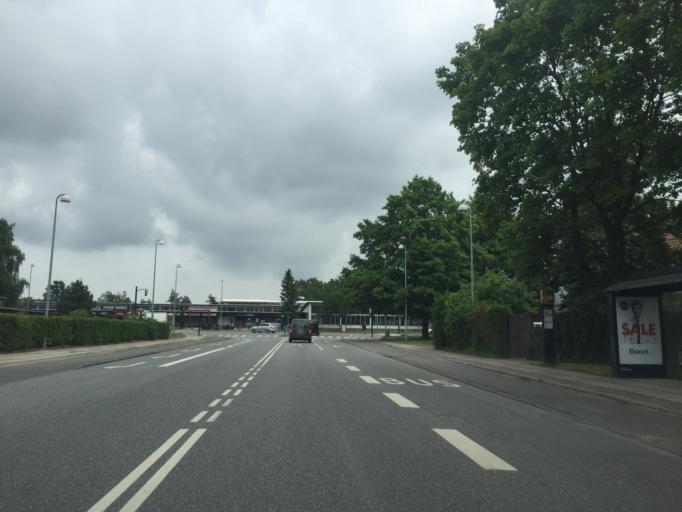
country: DK
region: Capital Region
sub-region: Gladsaxe Municipality
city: Buddinge
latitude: 55.7816
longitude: 12.4805
